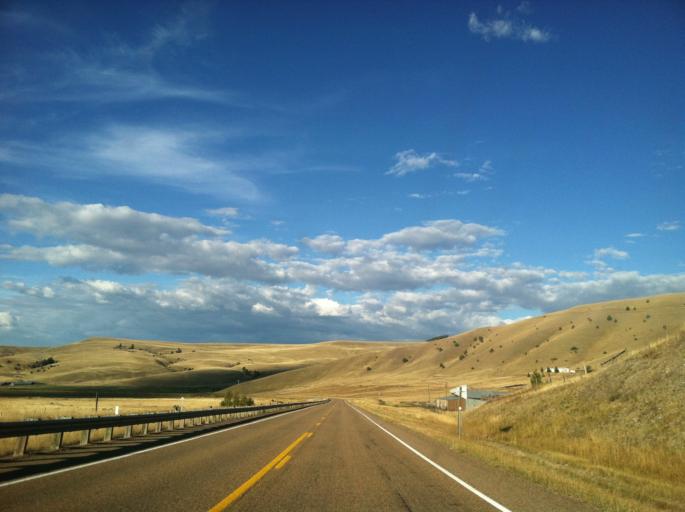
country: US
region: Montana
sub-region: Granite County
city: Philipsburg
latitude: 46.4901
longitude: -113.2275
